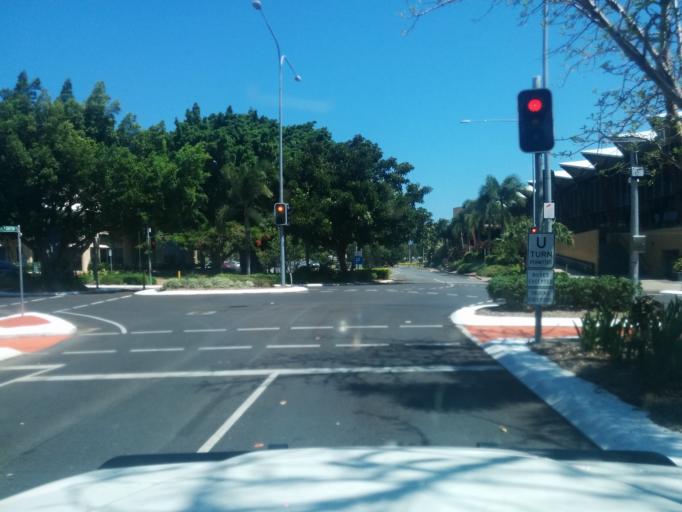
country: AU
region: Queensland
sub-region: Cairns
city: Cairns
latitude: -16.9263
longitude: 145.7777
